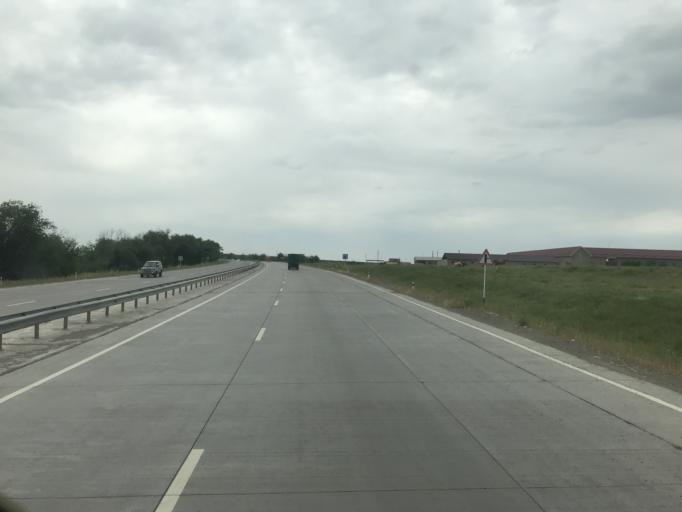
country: KZ
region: Ongtustik Qazaqstan
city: Shymkent
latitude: 42.2082
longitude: 69.5152
